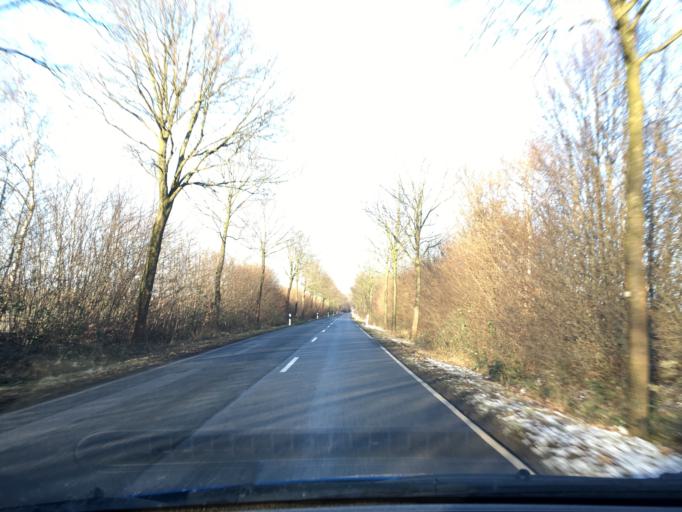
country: DE
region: Schleswig-Holstein
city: Schulendorf
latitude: 53.4635
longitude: 10.5624
